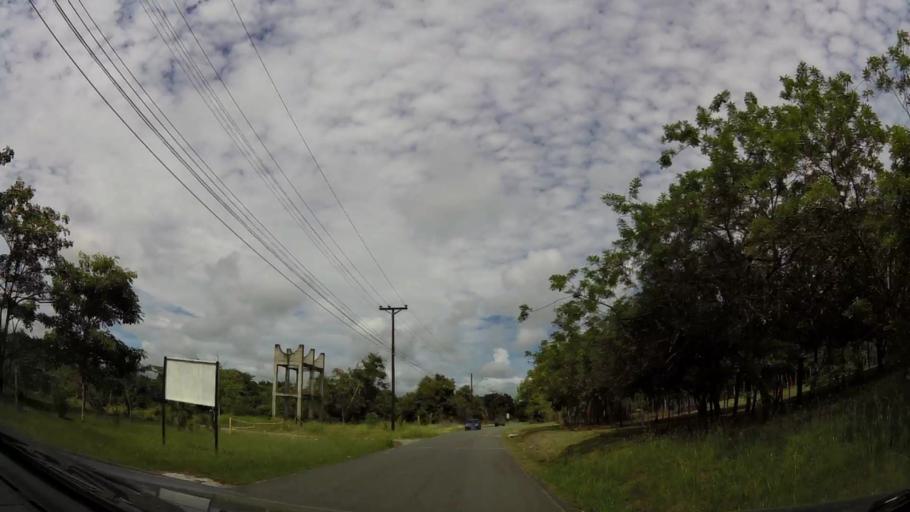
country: PA
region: Panama
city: Nueva Gorgona
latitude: 8.5320
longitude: -79.9177
